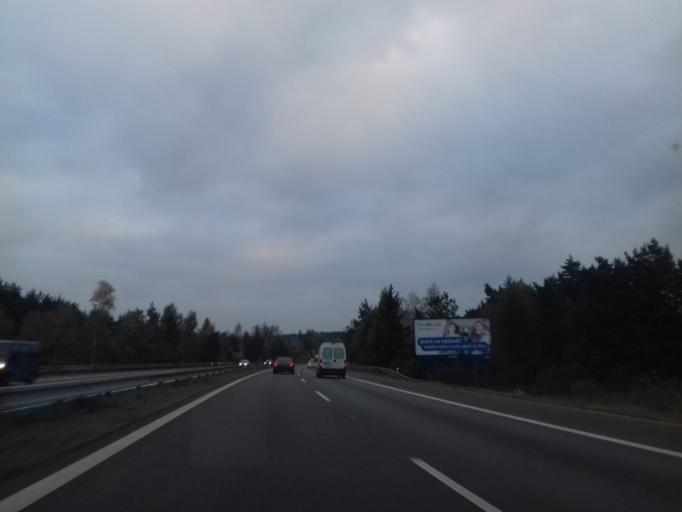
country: CZ
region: Central Bohemia
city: Zruc nad Sazavou
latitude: 49.7017
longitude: 15.0899
